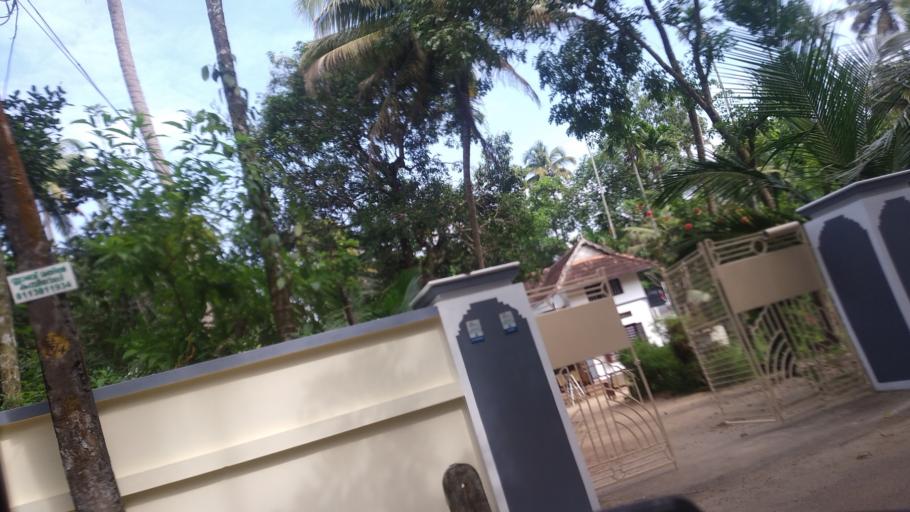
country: IN
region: Kerala
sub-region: Ernakulam
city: Elur
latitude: 10.0908
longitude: 76.2083
